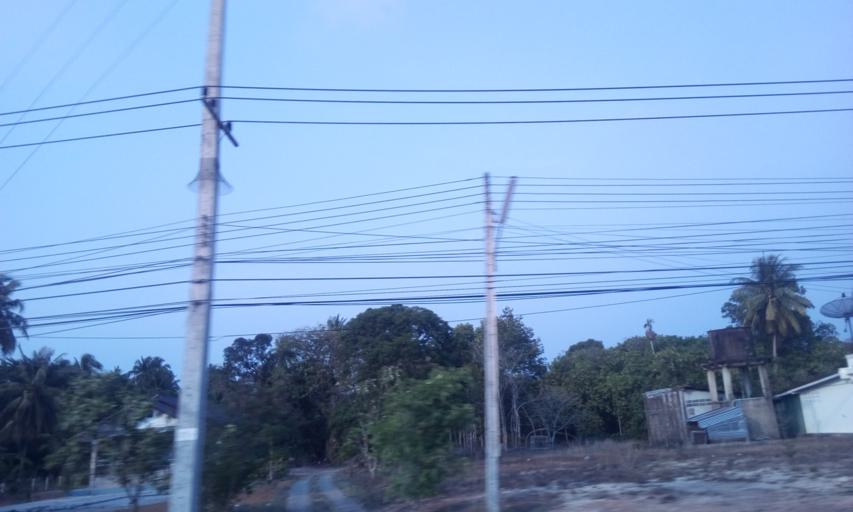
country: TH
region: Trat
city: Khao Saming
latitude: 12.4110
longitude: 102.3324
